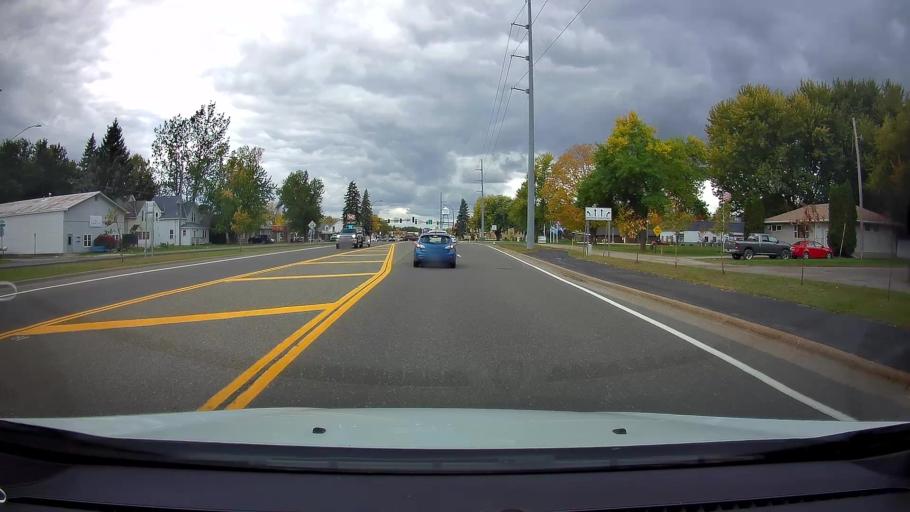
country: US
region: Minnesota
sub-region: Chisago County
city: Lindstrom
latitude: 45.3905
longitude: -92.8394
